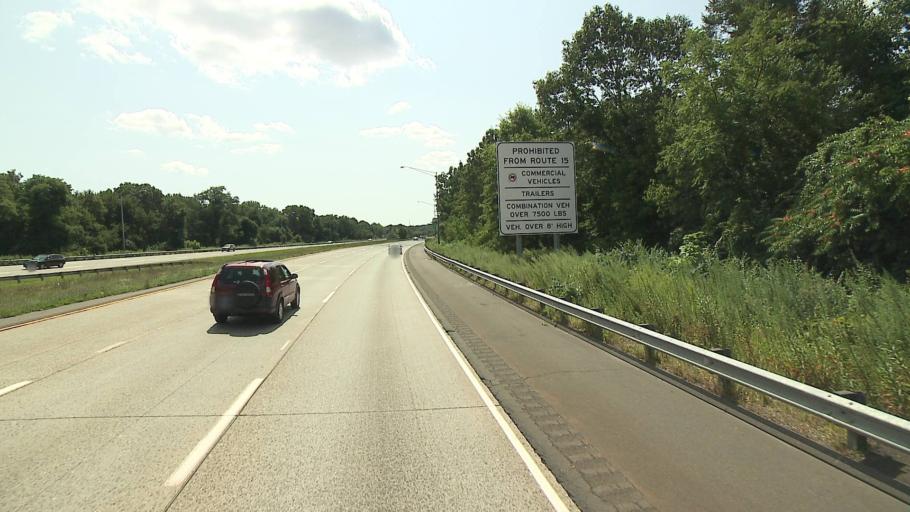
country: US
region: Connecticut
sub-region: Fairfield County
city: Trumbull
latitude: 41.2451
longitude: -73.1900
